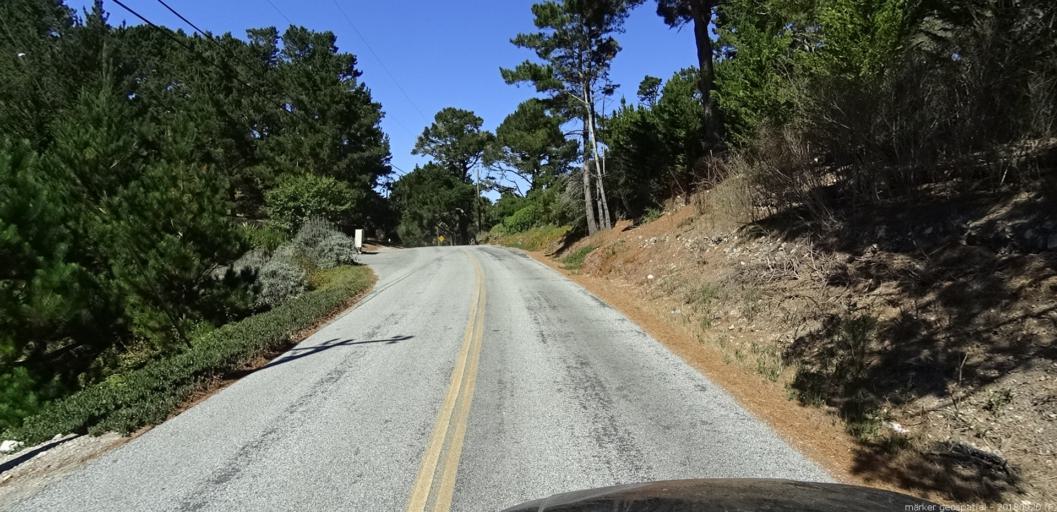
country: US
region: California
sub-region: Monterey County
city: Carmel-by-the-Sea
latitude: 36.5690
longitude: -121.8997
